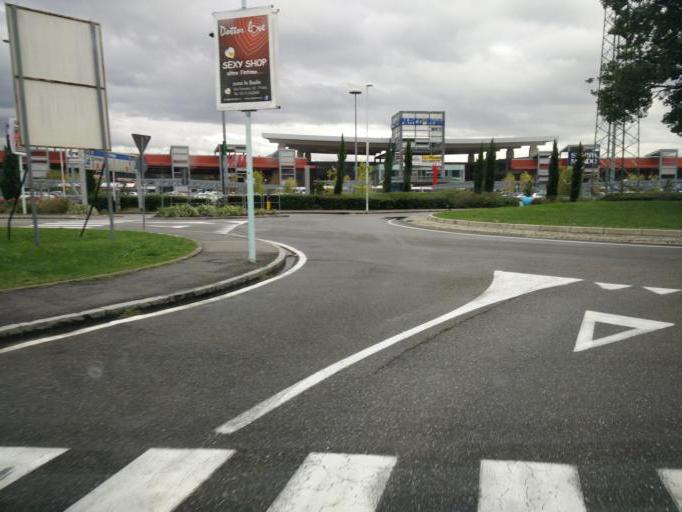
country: IT
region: Tuscany
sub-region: Provincia di Prato
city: Prato
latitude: 43.8747
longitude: 11.0636
